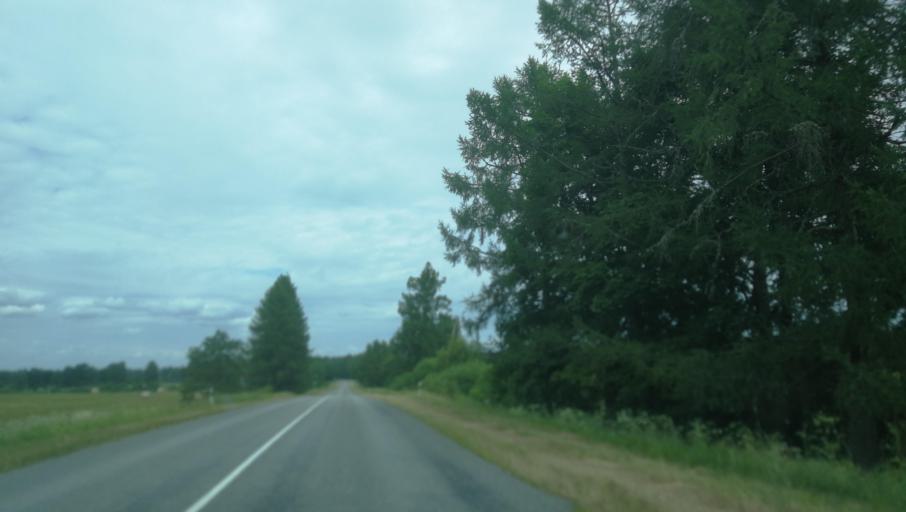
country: LV
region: Valmieras Rajons
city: Valmiera
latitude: 57.6832
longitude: 25.4301
